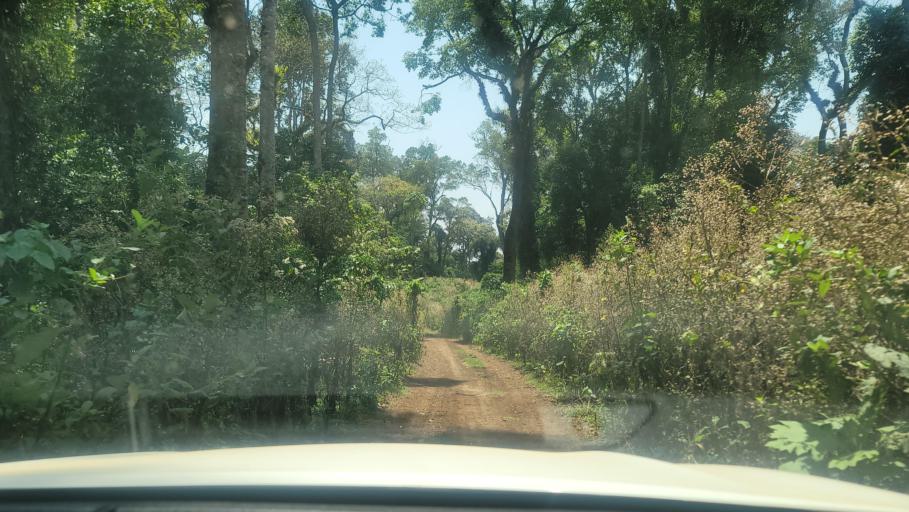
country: ET
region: Southern Nations, Nationalities, and People's Region
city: Bonga
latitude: 7.5496
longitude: 36.1742
